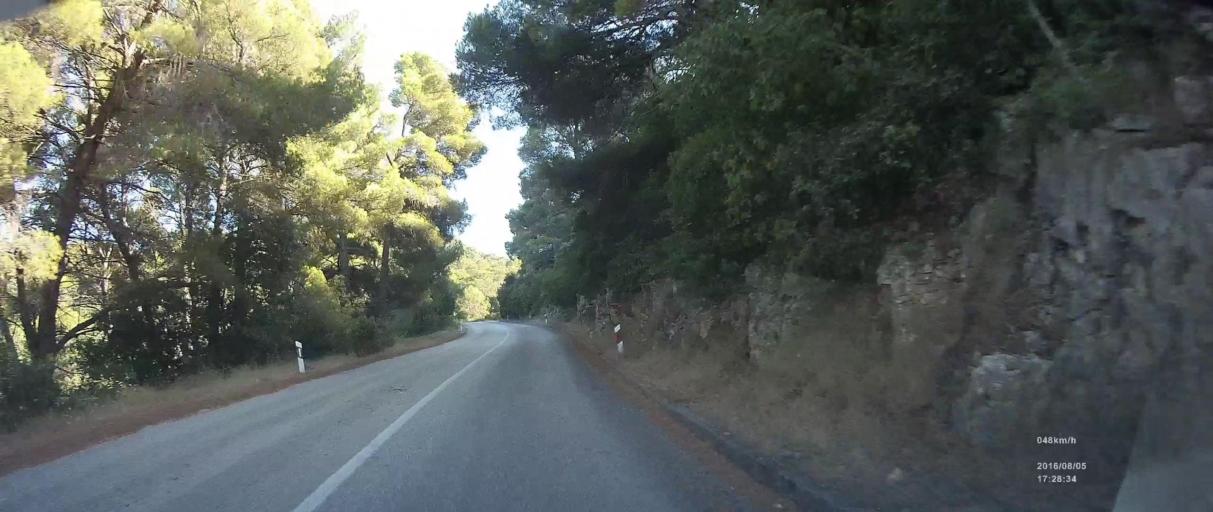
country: HR
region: Dubrovacko-Neretvanska
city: Blato
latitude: 42.7831
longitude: 17.4059
